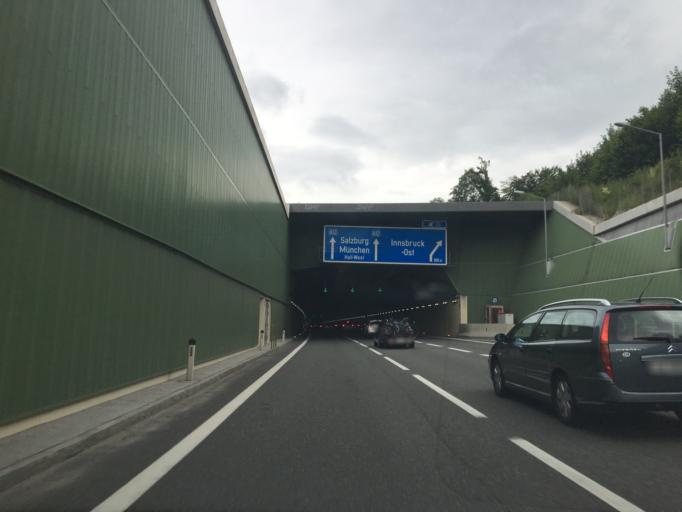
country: AT
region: Tyrol
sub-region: Politischer Bezirk Innsbruck Land
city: Aldrans
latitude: 47.2553
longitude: 11.4239
